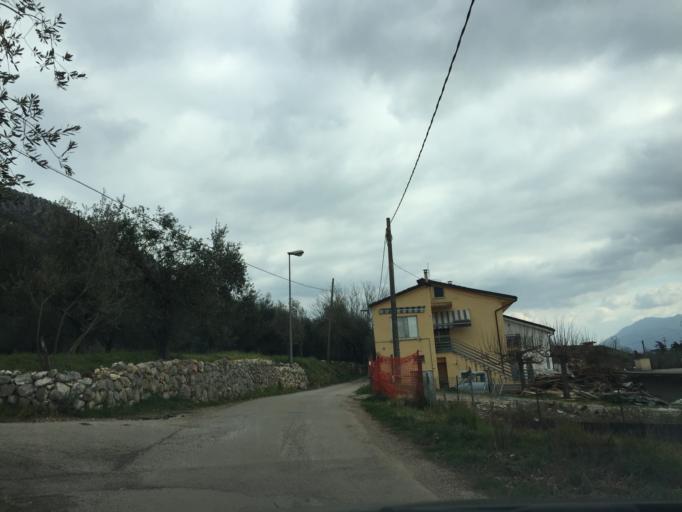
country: IT
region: Latium
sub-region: Provincia di Frosinone
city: Cassino
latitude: 41.4827
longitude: 13.8024
